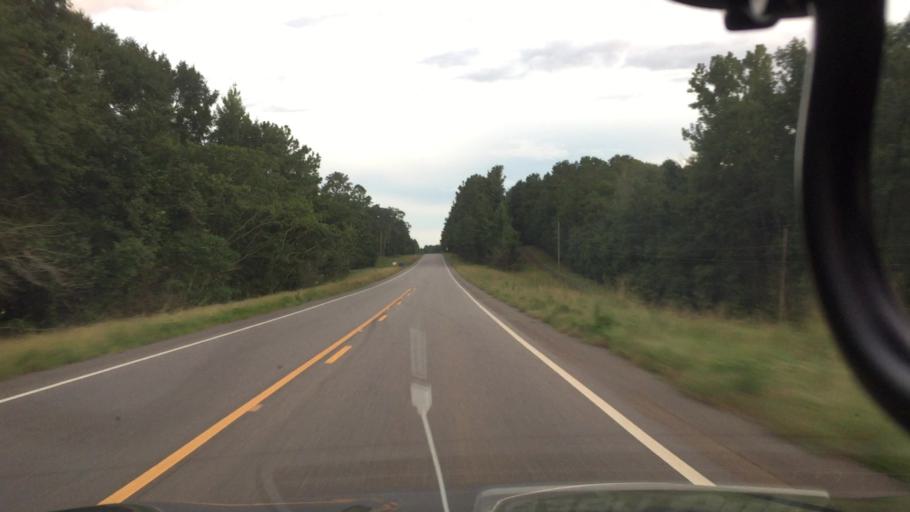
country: US
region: Alabama
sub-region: Pike County
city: Brundidge
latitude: 31.6108
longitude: -85.9465
